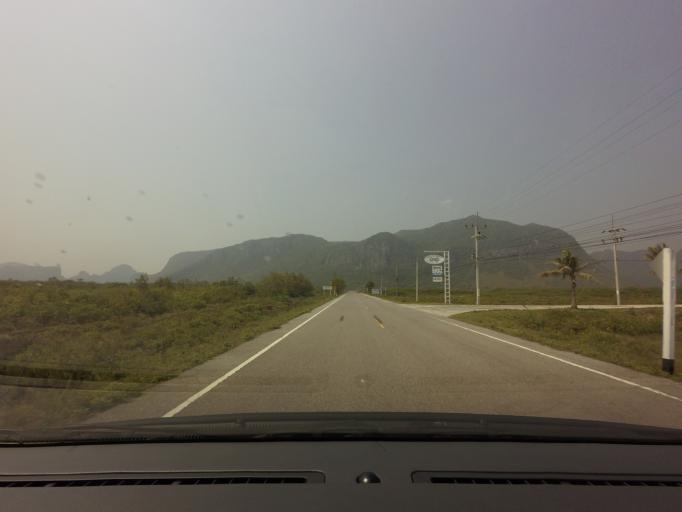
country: TH
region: Prachuap Khiri Khan
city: Sam Roi Yot
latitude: 12.1697
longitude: 99.9814
